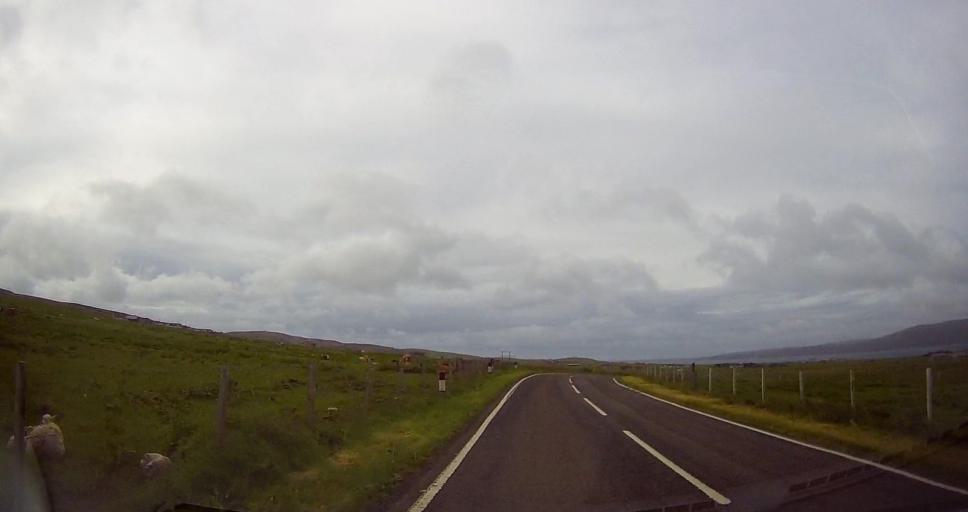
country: GB
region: Scotland
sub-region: Orkney Islands
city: Stromness
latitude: 58.9468
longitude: -3.2149
